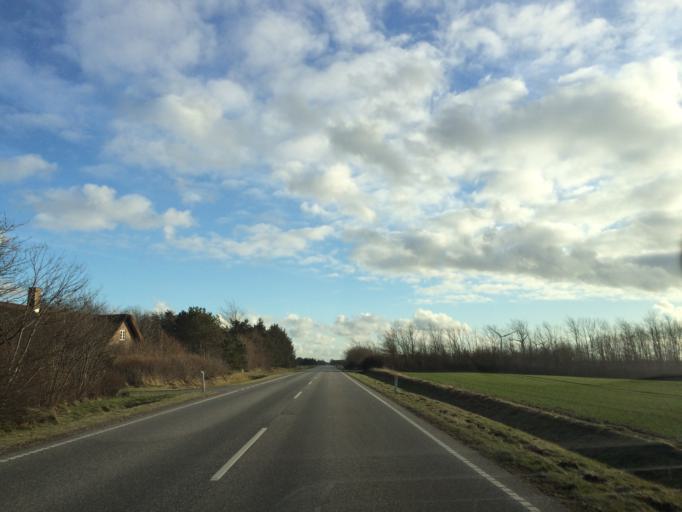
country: DK
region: Central Jutland
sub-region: Holstebro Kommune
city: Ulfborg
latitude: 56.3954
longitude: 8.3197
